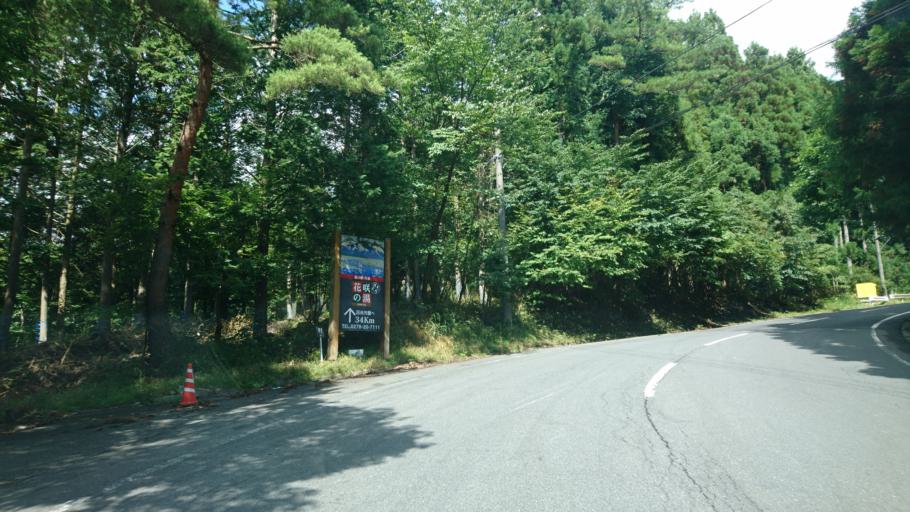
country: JP
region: Gunma
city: Omamacho-omama
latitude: 36.5724
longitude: 139.2354
